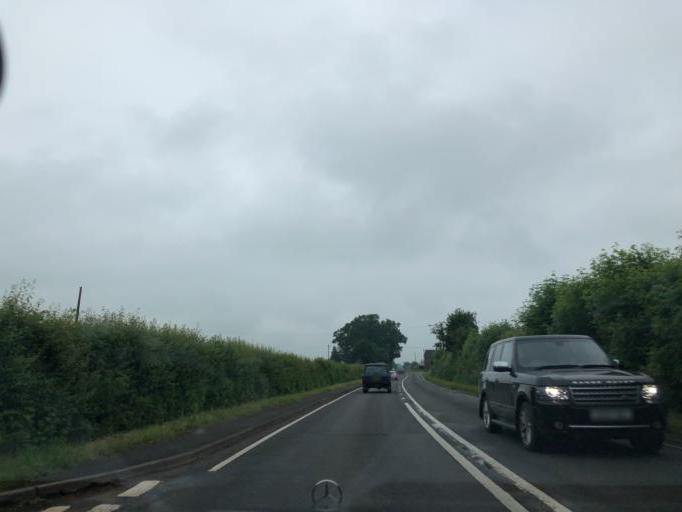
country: GB
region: England
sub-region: Warwickshire
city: Wroxall
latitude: 52.3069
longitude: -1.6608
